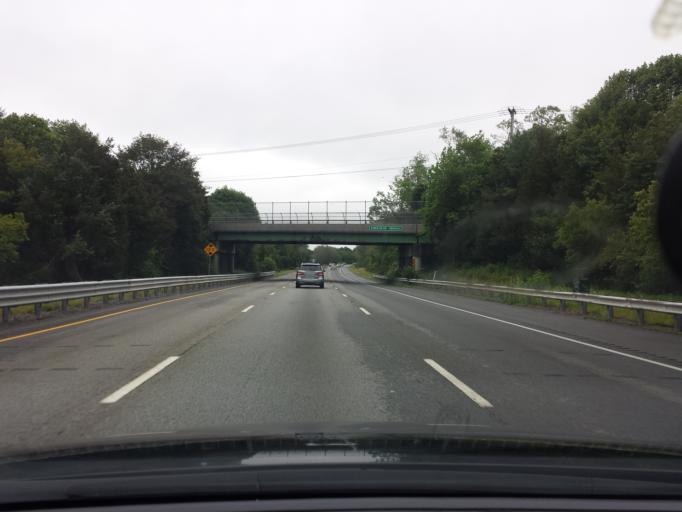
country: US
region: Rhode Island
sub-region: Bristol County
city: Warren
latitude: 41.7702
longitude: -71.2477
